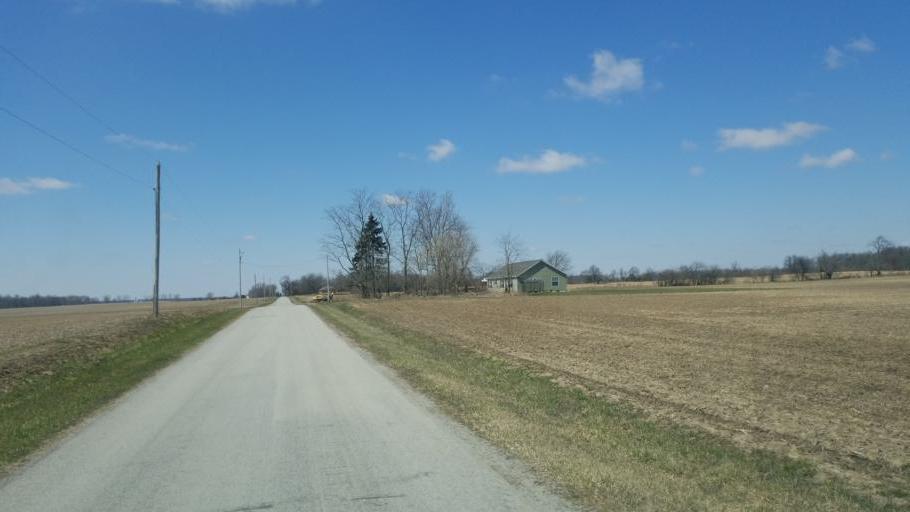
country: US
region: Ohio
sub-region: Marion County
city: Marion
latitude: 40.7245
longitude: -83.1385
